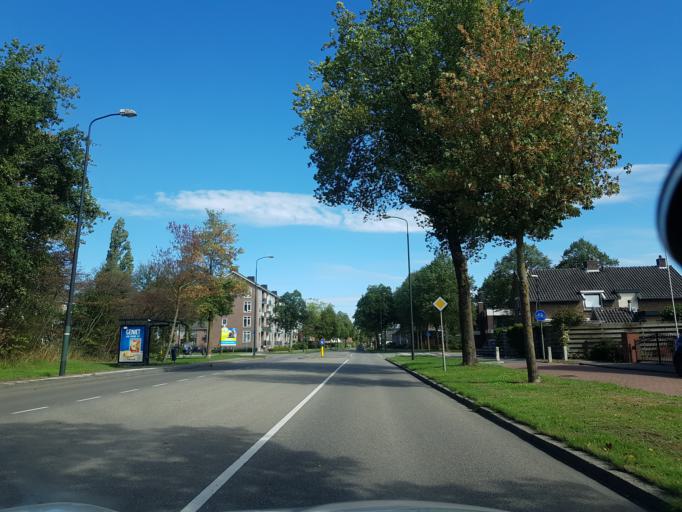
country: NL
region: Gelderland
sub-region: Gemeente Apeldoorn
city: Apeldoorn
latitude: 52.1918
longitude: 5.9539
